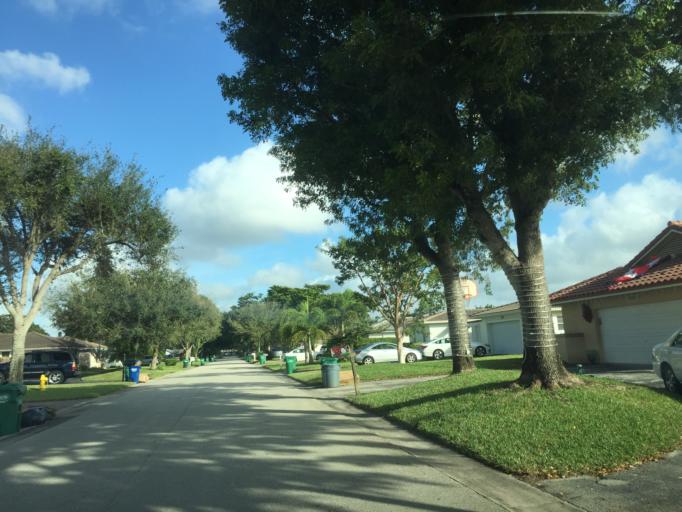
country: US
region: Florida
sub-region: Broward County
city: North Lauderdale
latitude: 26.2405
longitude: -80.2347
